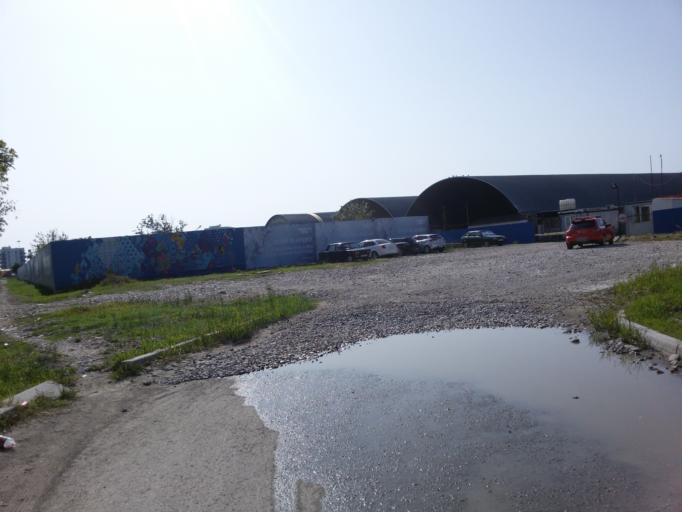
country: RU
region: Krasnodarskiy
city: Adler
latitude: 43.4160
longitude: 39.9392
